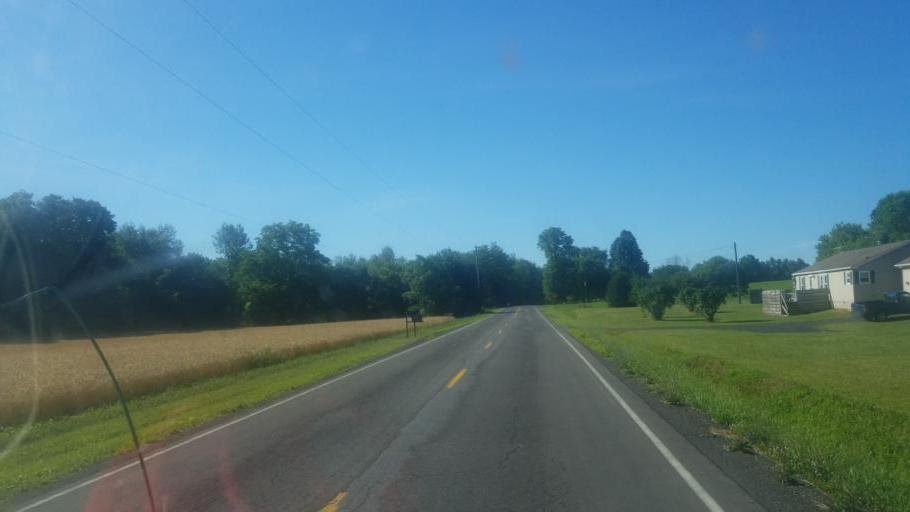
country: US
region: New York
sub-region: Ontario County
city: Clifton Springs
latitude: 42.8533
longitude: -77.1101
